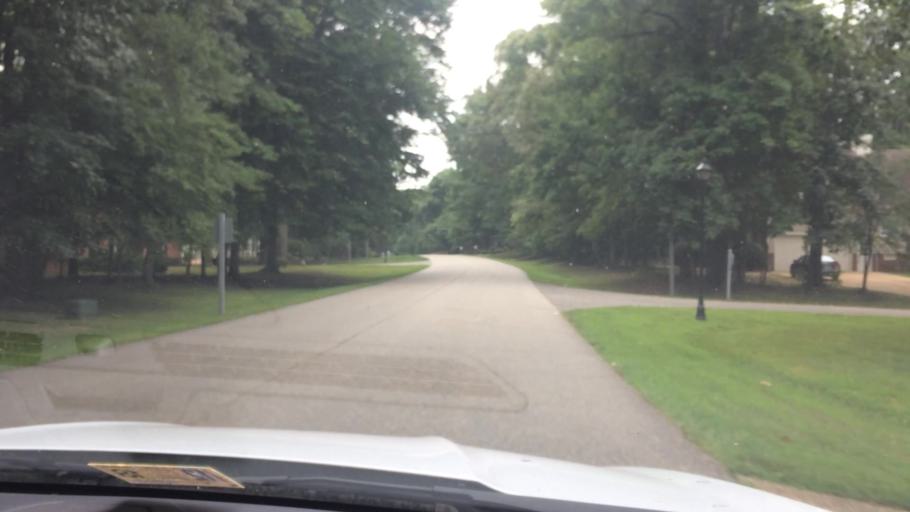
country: US
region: Virginia
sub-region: James City County
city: Williamsburg
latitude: 37.3073
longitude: -76.7713
